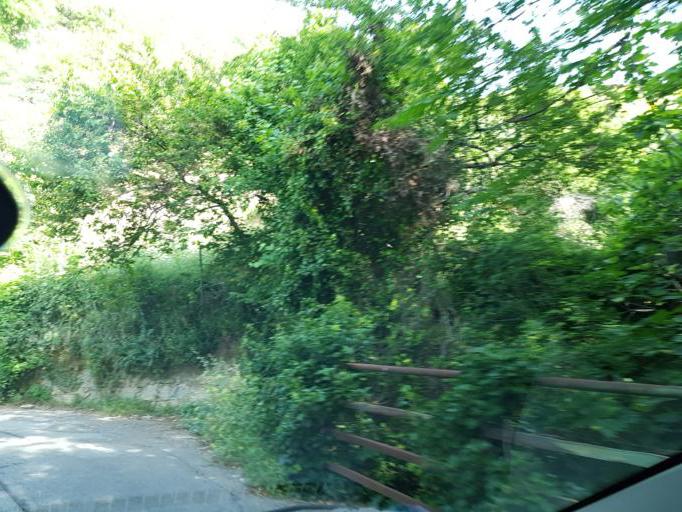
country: IT
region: Liguria
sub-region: Provincia di Genova
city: Genoa
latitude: 44.4284
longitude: 8.9162
